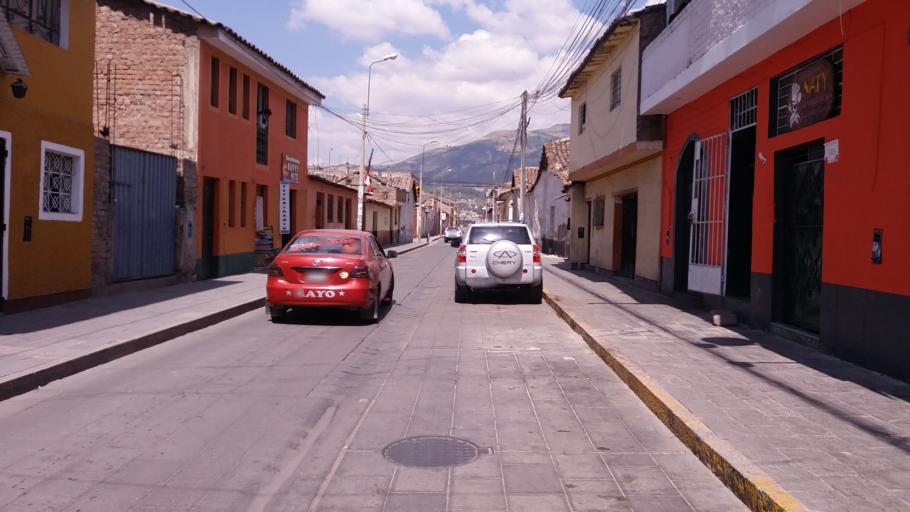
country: PE
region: Ayacucho
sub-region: Provincia de Huamanga
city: Ayacucho
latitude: -13.1585
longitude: -74.2235
